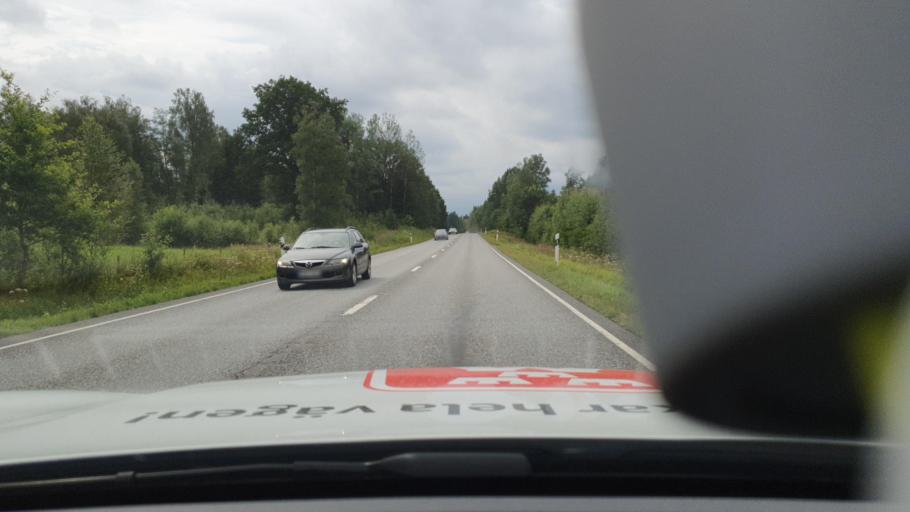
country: SE
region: Joenkoeping
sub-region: Gislaveds Kommun
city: Gislaved
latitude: 57.2585
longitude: 13.4778
